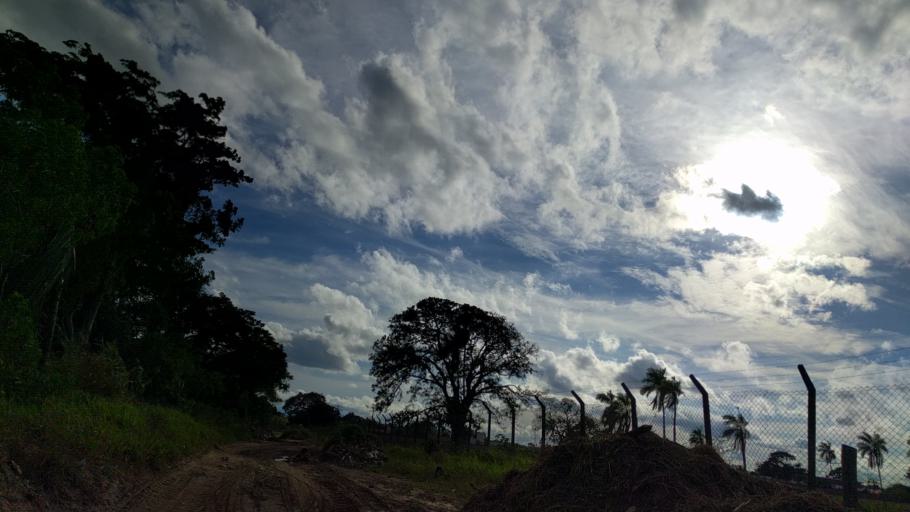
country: BO
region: Santa Cruz
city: Santa Cruz de la Sierra
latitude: -17.8551
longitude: -63.2673
